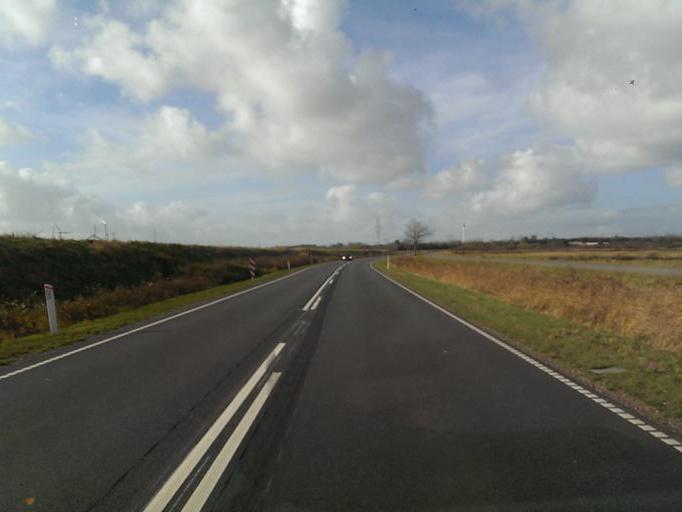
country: DK
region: South Denmark
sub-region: Esbjerg Kommune
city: Tjaereborg
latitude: 55.4648
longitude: 8.5426
